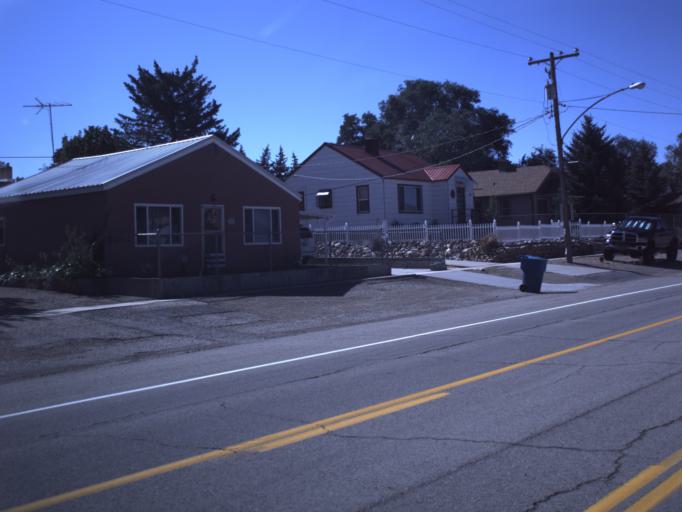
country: US
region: Utah
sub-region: Tooele County
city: Tooele
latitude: 40.4529
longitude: -112.3619
